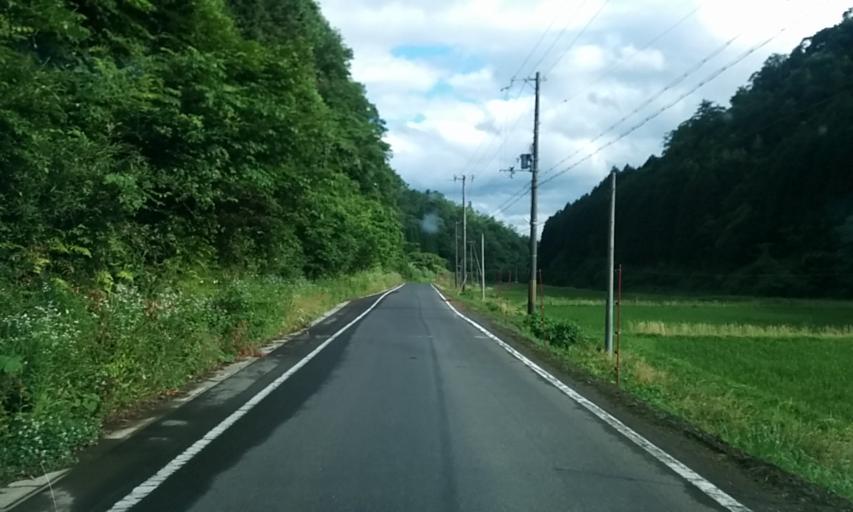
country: JP
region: Kyoto
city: Ayabe
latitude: 35.3698
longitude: 135.2881
